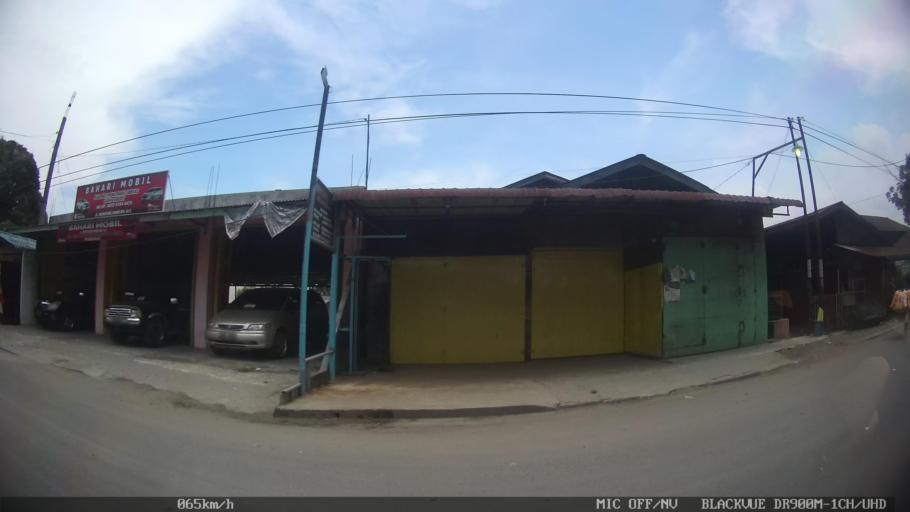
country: ID
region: North Sumatra
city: Labuhan Deli
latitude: 3.7038
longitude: 98.6785
